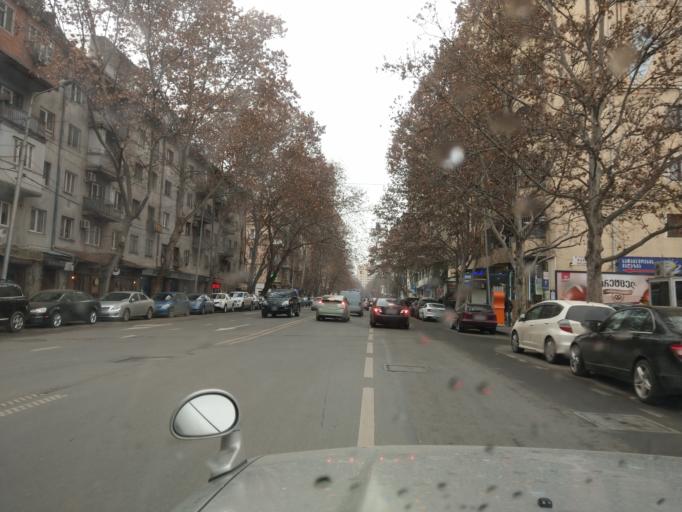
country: GE
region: T'bilisi
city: Tbilisi
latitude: 41.7220
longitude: 44.7682
